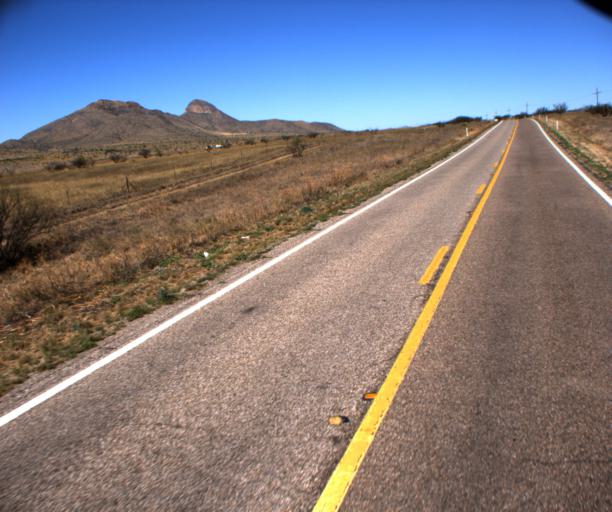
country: US
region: Arizona
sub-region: Cochise County
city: Huachuca City
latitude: 31.7078
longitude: -110.4437
